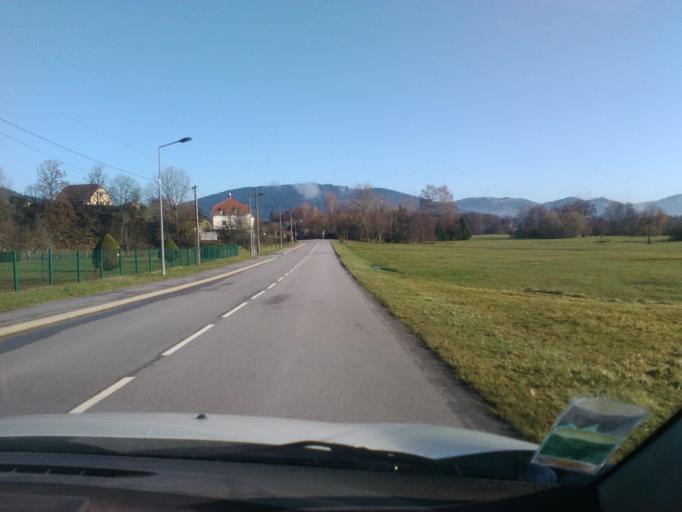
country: FR
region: Lorraine
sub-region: Departement des Vosges
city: Saint-Ame
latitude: 48.0155
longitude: 6.6492
